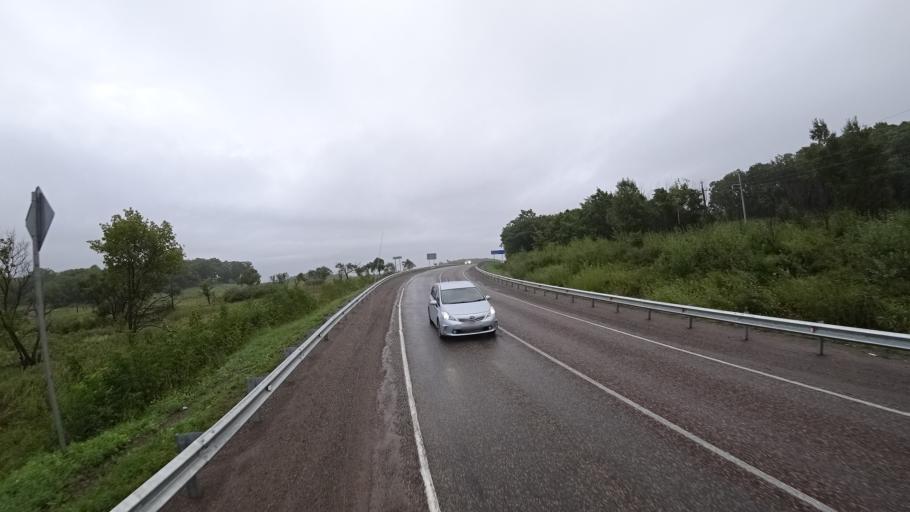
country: RU
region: Primorskiy
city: Monastyrishche
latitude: 44.2701
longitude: 132.4639
